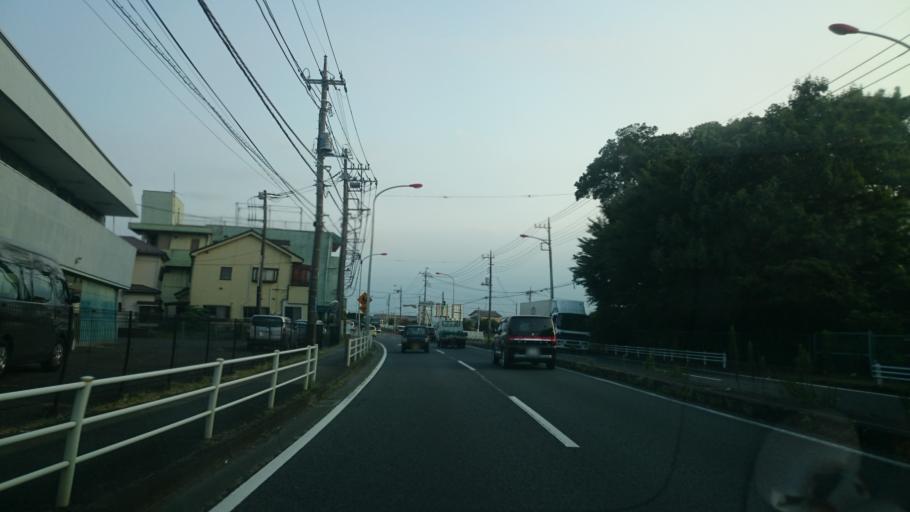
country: JP
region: Saitama
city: Kasukabe
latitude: 35.9770
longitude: 139.7361
